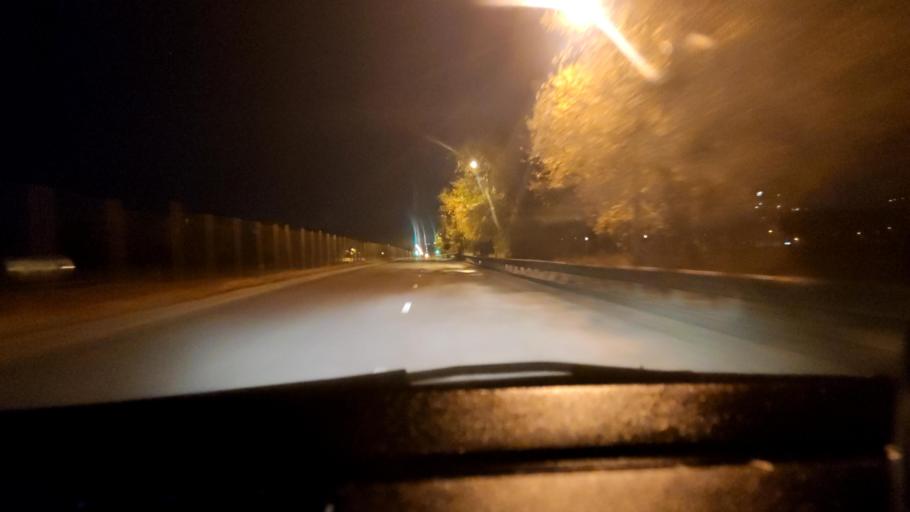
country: RU
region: Voronezj
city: Voronezh
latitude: 51.7071
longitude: 39.2262
